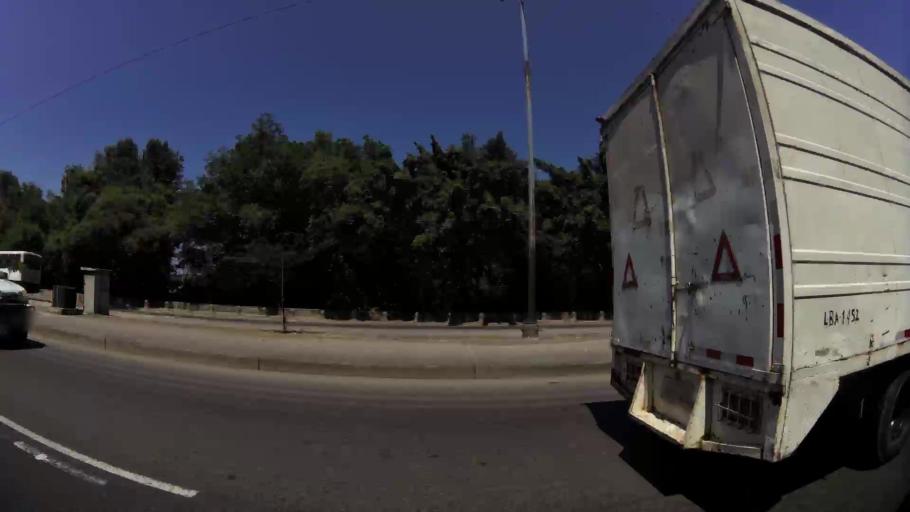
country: EC
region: Guayas
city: Guayaquil
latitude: -2.1886
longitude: -79.9201
